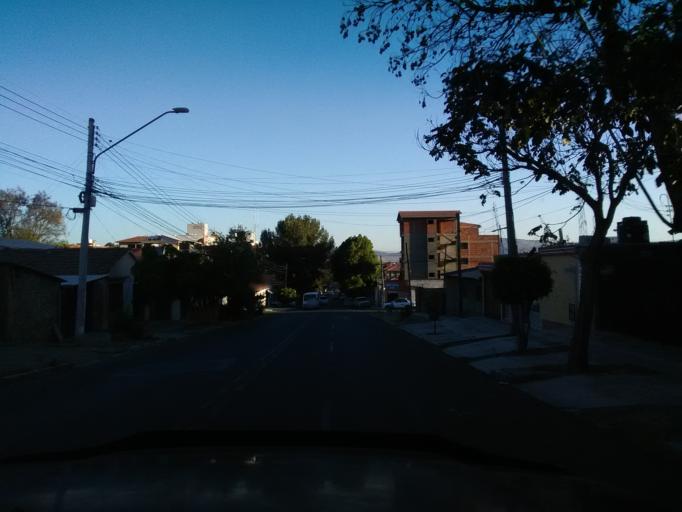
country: BO
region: Cochabamba
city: Cochabamba
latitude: -17.3679
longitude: -66.1510
